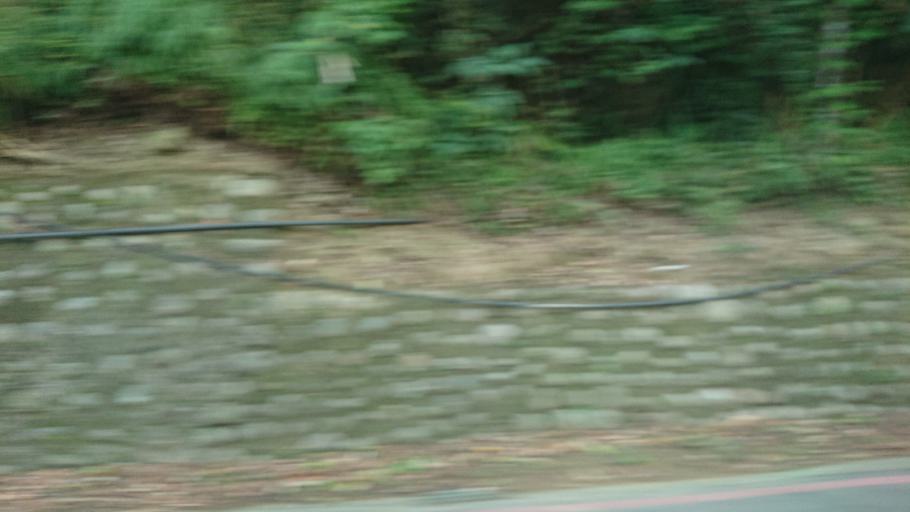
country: TW
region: Taiwan
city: Daxi
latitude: 24.8694
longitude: 121.4120
